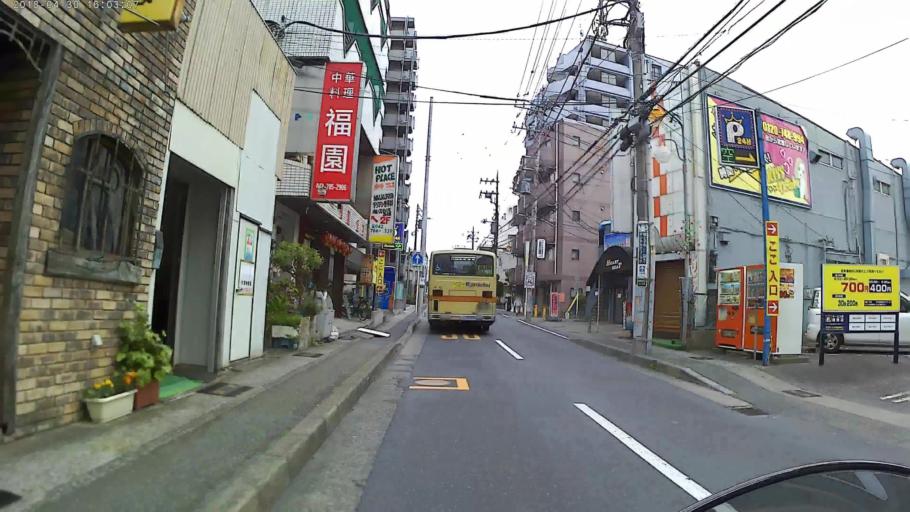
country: JP
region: Tokyo
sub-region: Machida-shi
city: Machida
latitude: 35.5136
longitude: 139.4217
